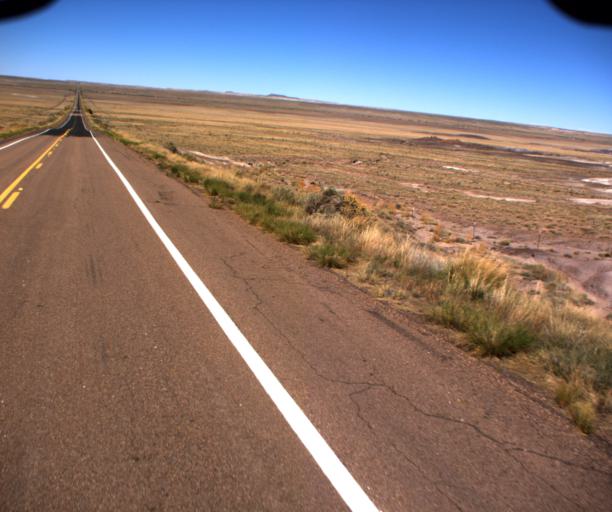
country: US
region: Arizona
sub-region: Navajo County
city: Snowflake
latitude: 34.7167
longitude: -109.7688
